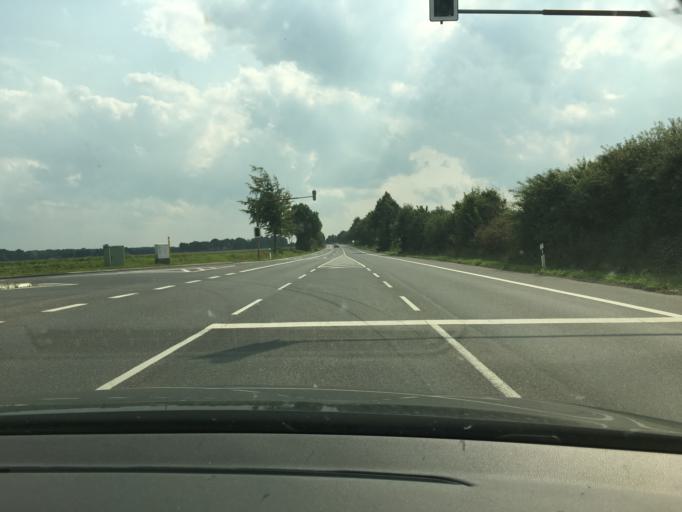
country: DE
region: North Rhine-Westphalia
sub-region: Regierungsbezirk Koln
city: Norvenich
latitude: 50.8209
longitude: 6.6334
